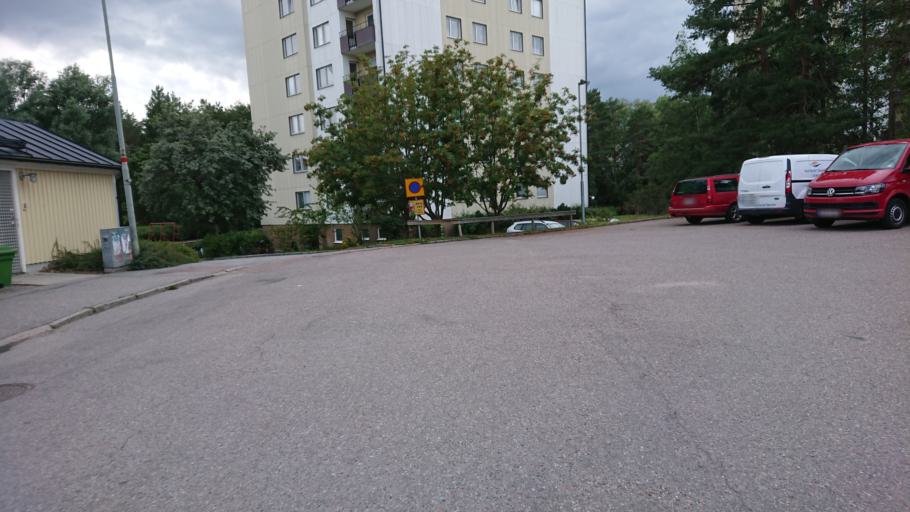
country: SE
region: Uppsala
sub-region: Uppsala Kommun
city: Uppsala
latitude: 59.8422
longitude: 17.6017
